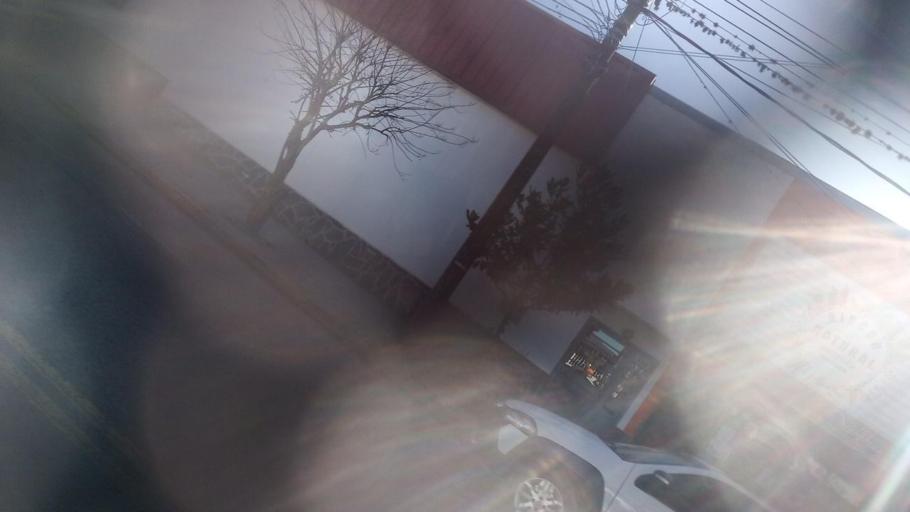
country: AR
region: Jujuy
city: San Salvador de Jujuy
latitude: -24.1706
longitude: -65.3115
